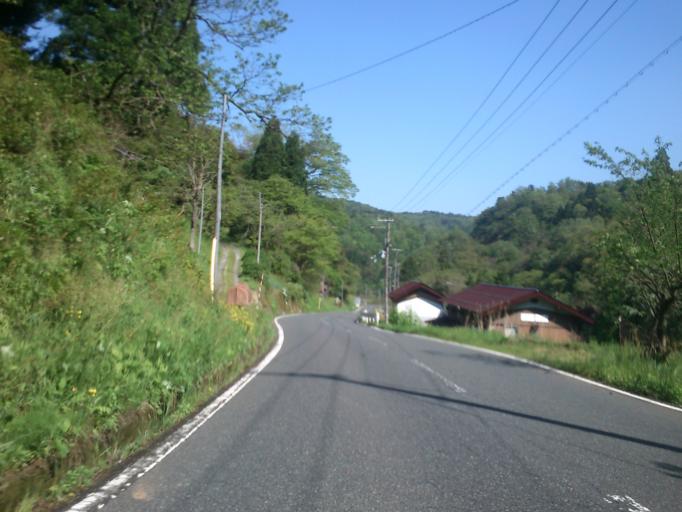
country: JP
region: Kyoto
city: Miyazu
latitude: 35.6275
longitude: 135.1263
